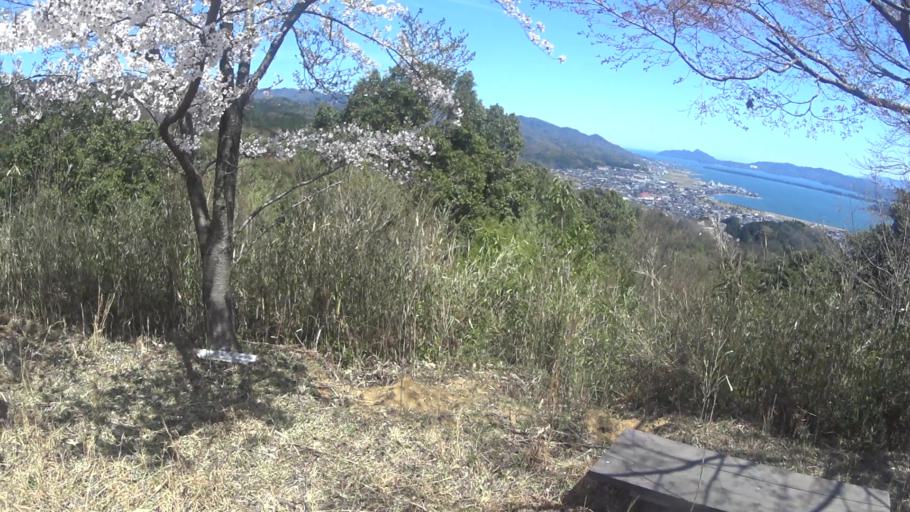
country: JP
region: Kyoto
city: Miyazu
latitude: 35.5642
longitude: 135.1379
